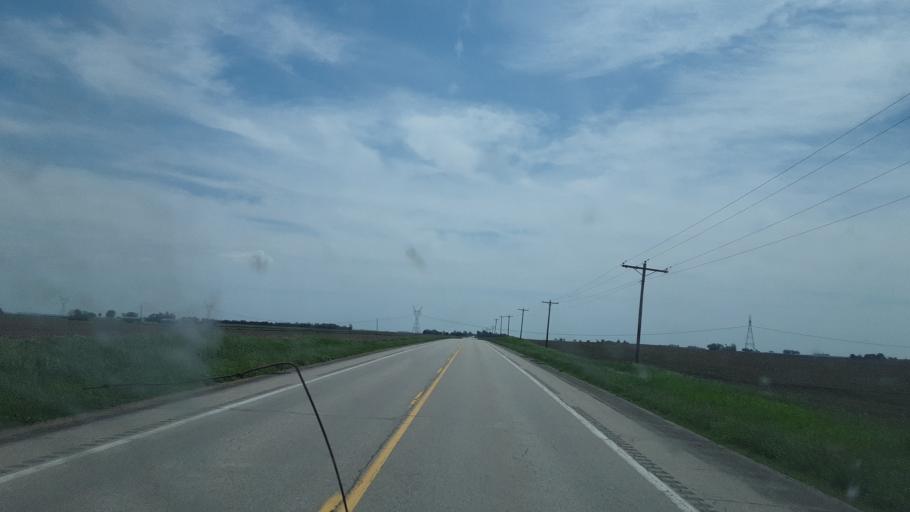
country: US
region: Illinois
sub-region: McLean County
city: Heyworth
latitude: 40.3122
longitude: -88.9435
